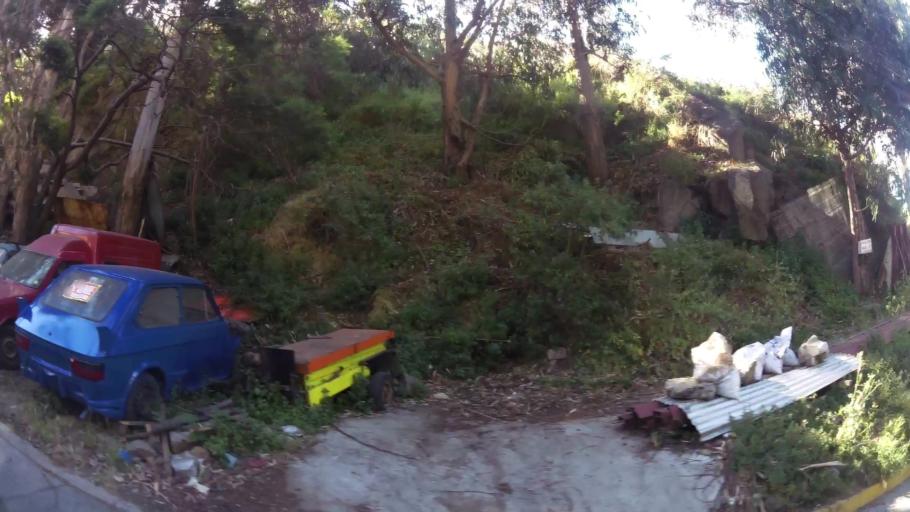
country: CL
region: Valparaiso
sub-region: Provincia de Valparaiso
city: Valparaiso
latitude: -33.0551
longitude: -71.6150
